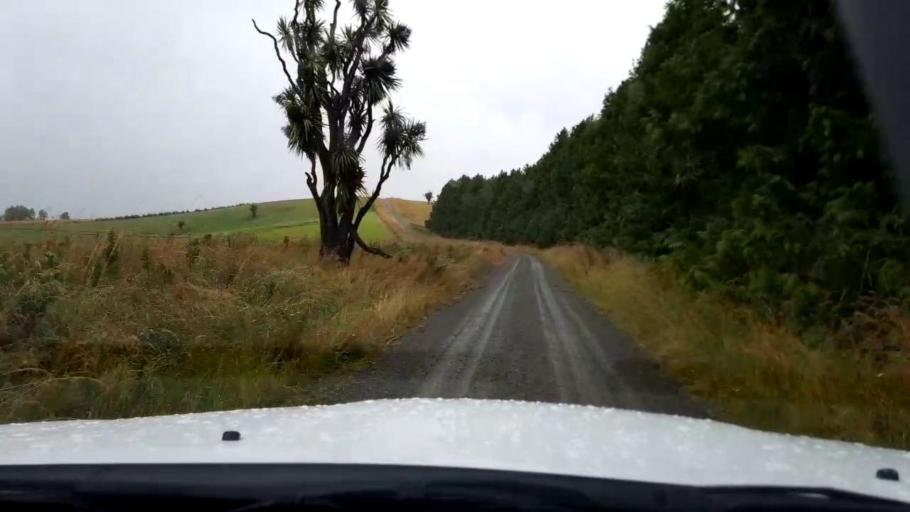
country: NZ
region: Canterbury
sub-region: Timaru District
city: Pleasant Point
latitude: -44.1729
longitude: 171.0954
